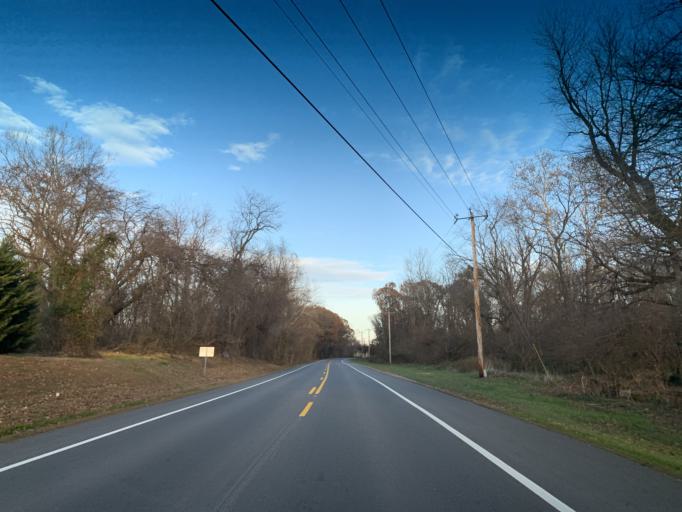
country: US
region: Maryland
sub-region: Kent County
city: Chestertown
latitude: 39.2962
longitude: -76.0716
